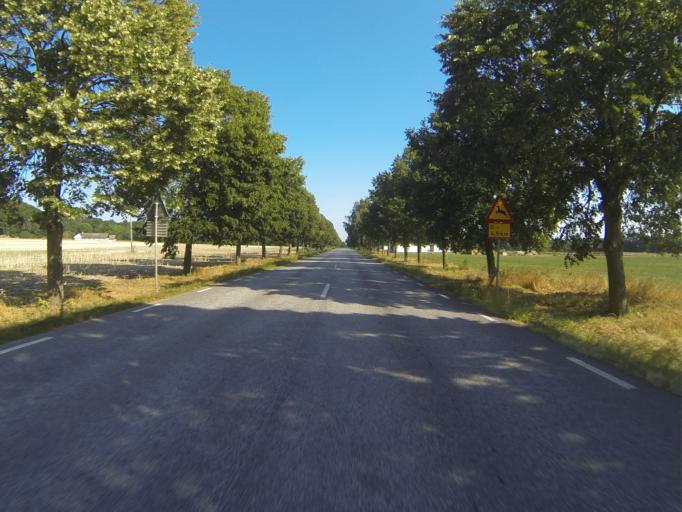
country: SE
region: Skane
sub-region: Hoors Kommun
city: Loberod
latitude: 55.7019
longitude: 13.5758
